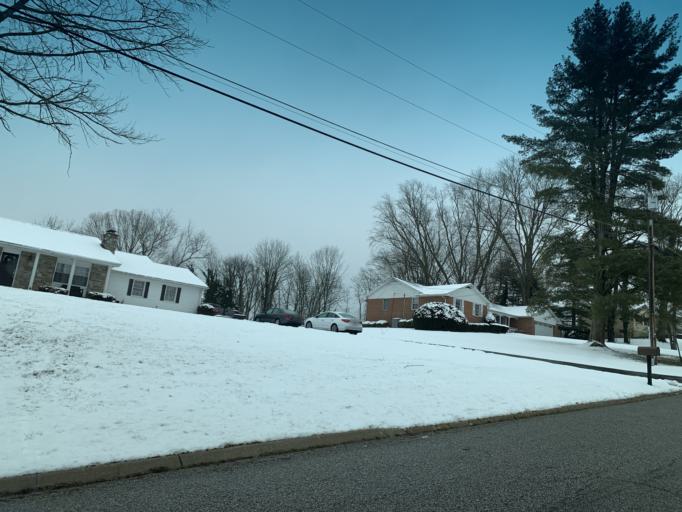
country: US
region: Maryland
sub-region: Harford County
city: Pleasant Hills
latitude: 39.5093
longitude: -76.3767
